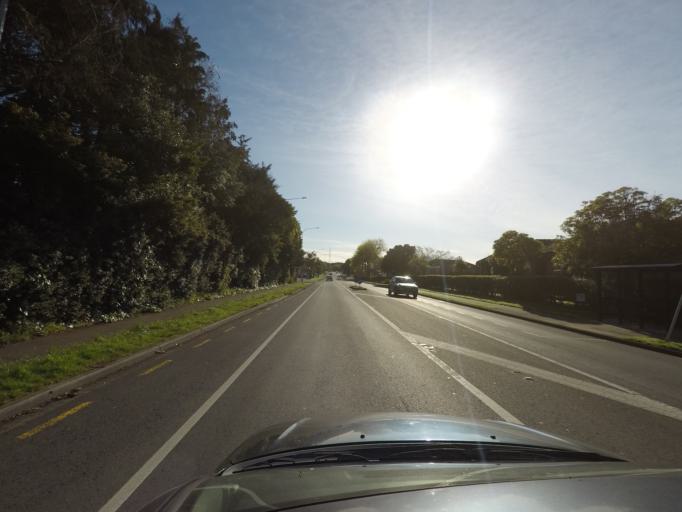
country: NZ
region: Auckland
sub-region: Auckland
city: Takanini
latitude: -37.0131
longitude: 174.9105
